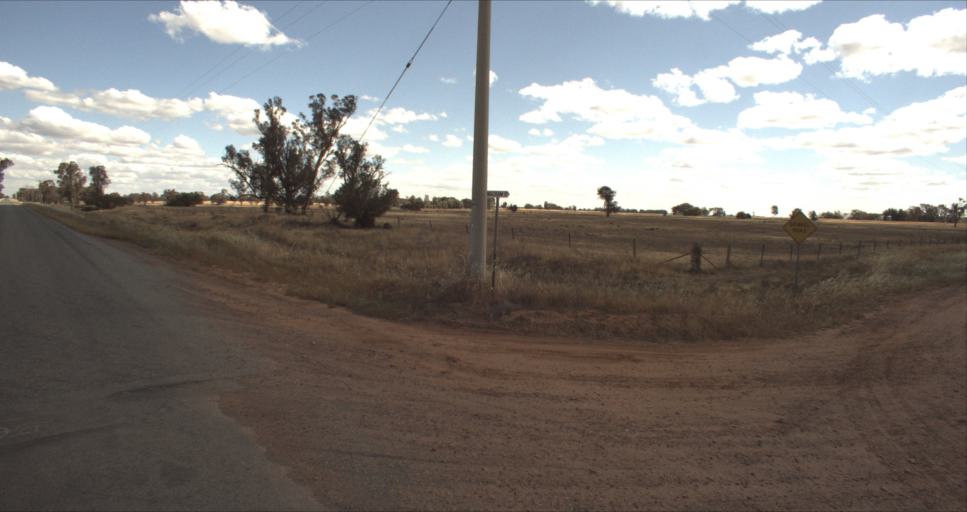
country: AU
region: New South Wales
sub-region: Leeton
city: Leeton
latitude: -34.4825
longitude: 146.2488
